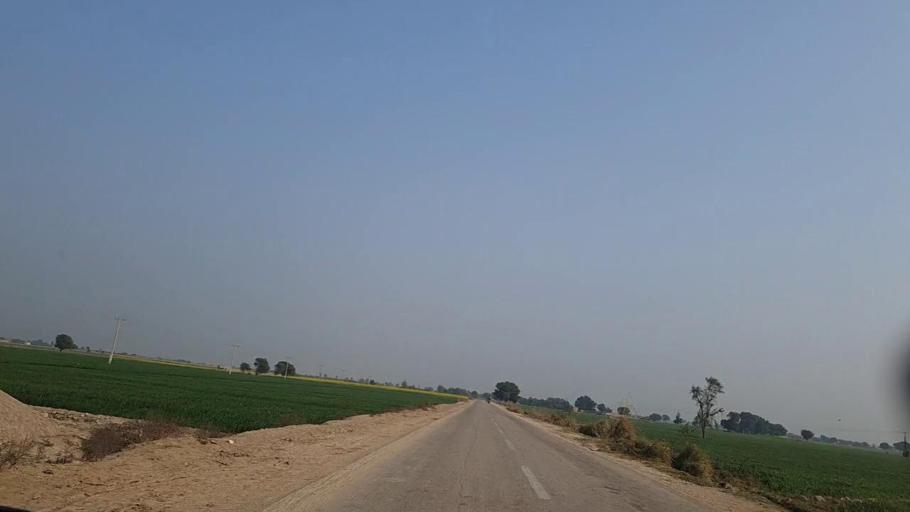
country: PK
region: Sindh
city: Sann
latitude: 26.1417
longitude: 68.1547
